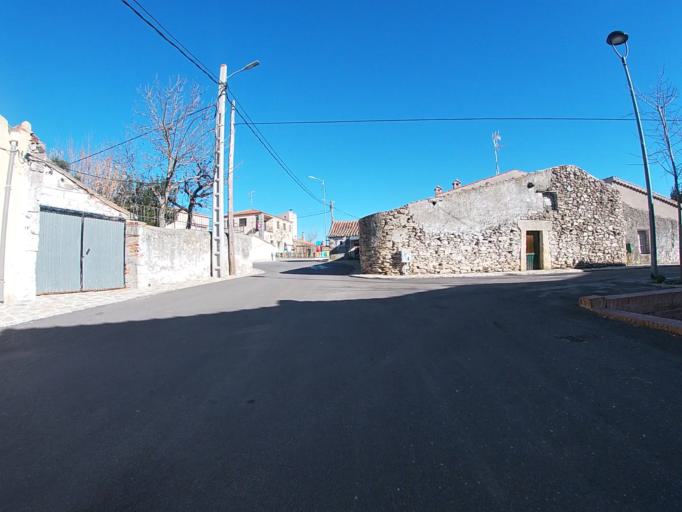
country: ES
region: Castille and Leon
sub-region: Provincia de Salamanca
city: Juzbado
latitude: 41.0776
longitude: -5.8616
